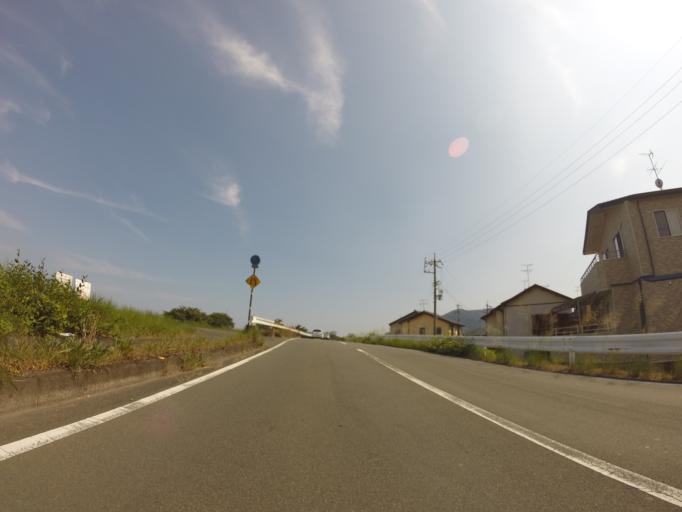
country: JP
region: Shizuoka
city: Shizuoka-shi
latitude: 34.9872
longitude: 138.3548
